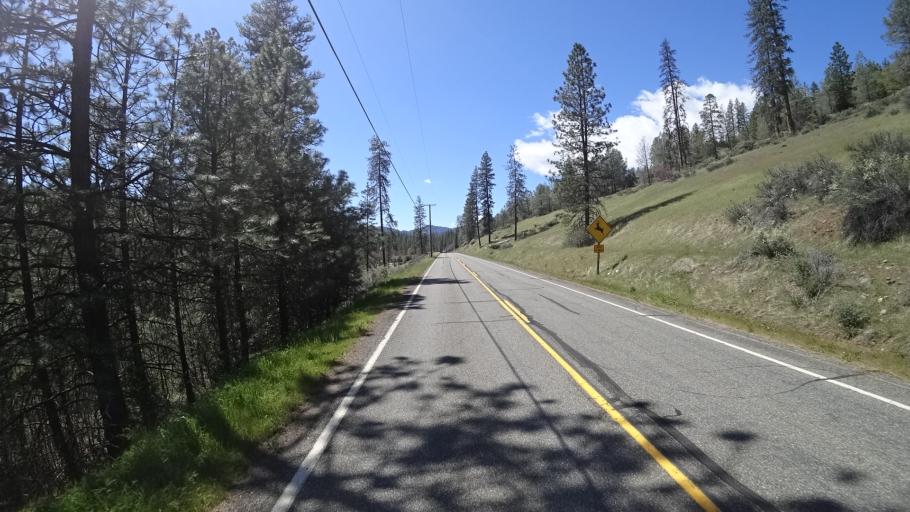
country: US
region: California
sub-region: Trinity County
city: Weaverville
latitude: 40.7502
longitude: -122.8899
